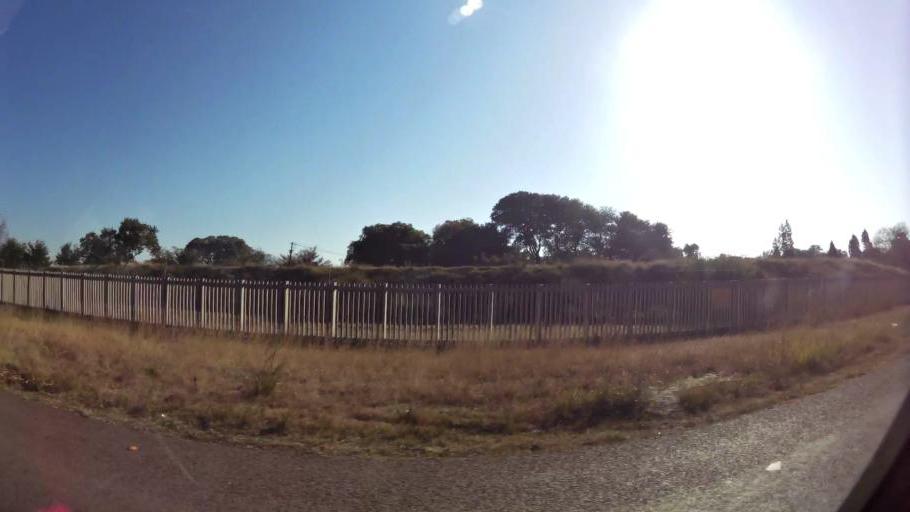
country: ZA
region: Gauteng
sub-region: City of Tshwane Metropolitan Municipality
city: Pretoria
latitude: -25.6568
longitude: 28.1779
